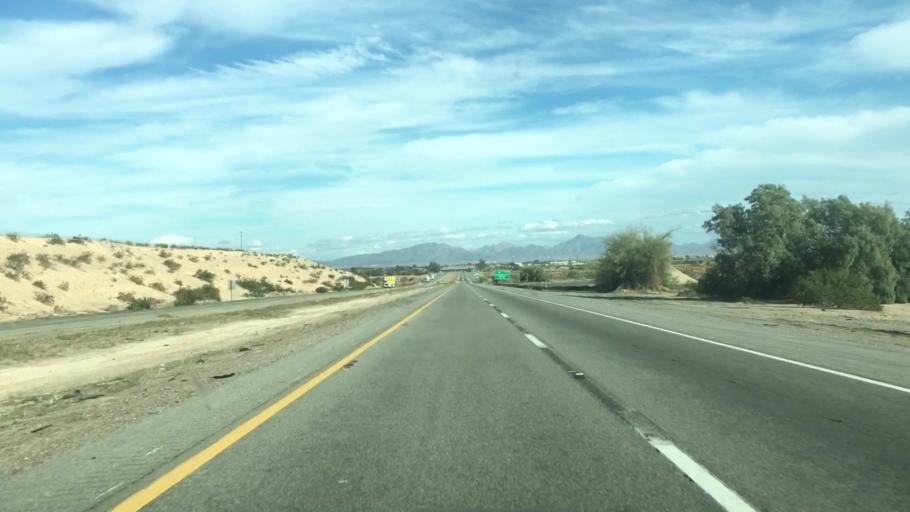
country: US
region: California
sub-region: Riverside County
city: Mesa Verde
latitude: 33.6066
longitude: -114.6747
